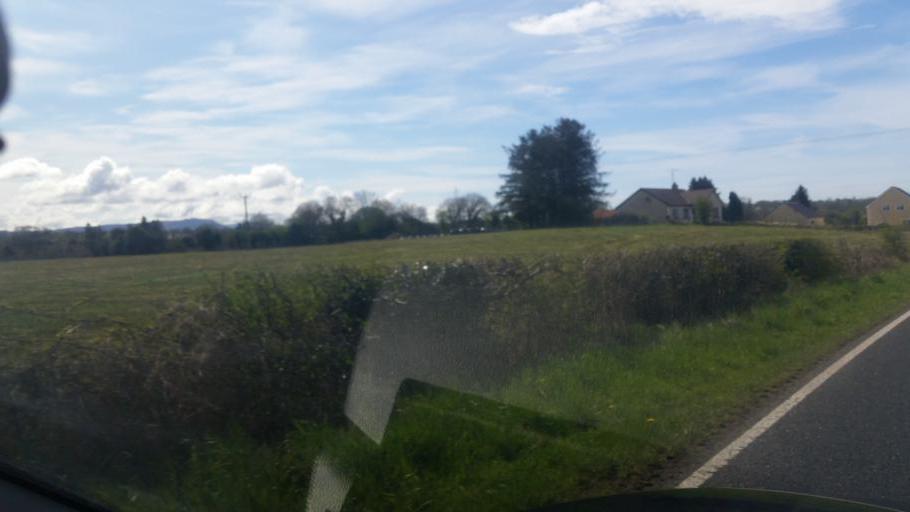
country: IE
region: Ulster
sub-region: County Donegal
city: Ballyshannon
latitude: 54.4738
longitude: -8.0875
